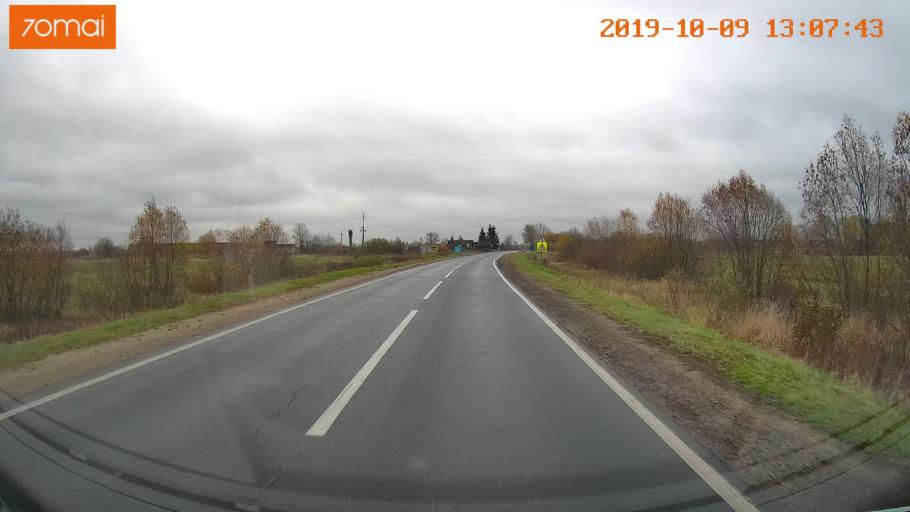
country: RU
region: Jaroslavl
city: Lyubim
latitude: 58.3569
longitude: 40.6497
